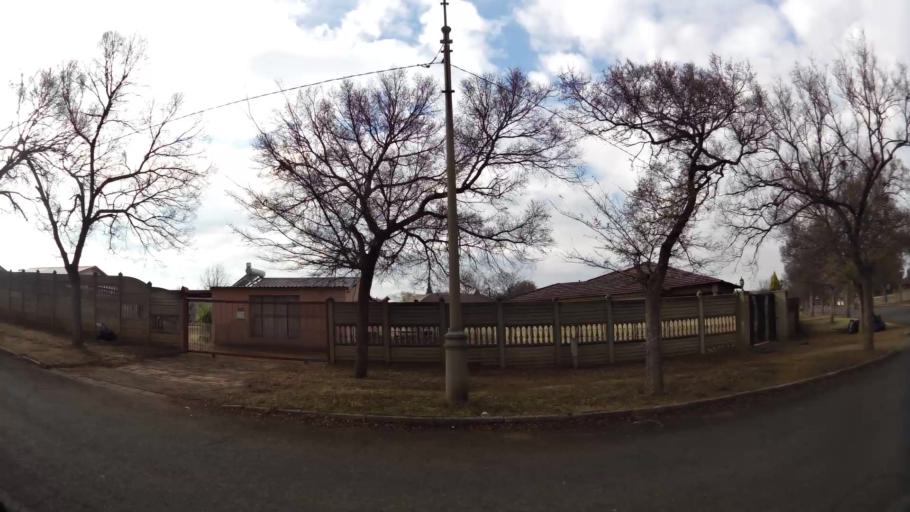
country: ZA
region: Gauteng
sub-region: Sedibeng District Municipality
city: Vanderbijlpark
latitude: -26.6948
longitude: 27.8141
